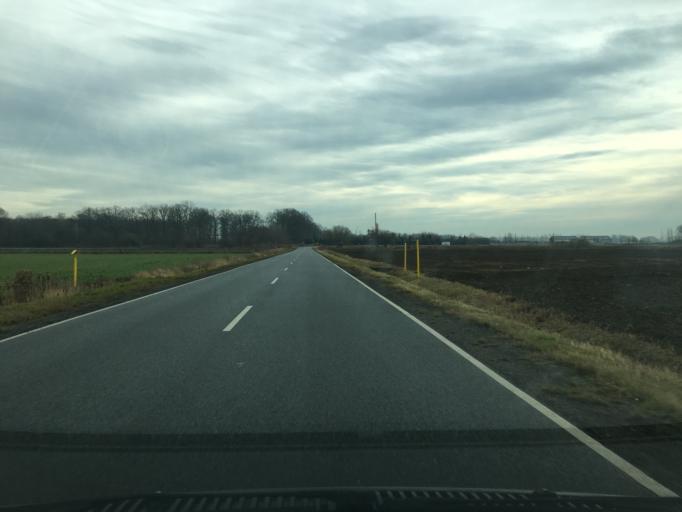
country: PL
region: Lower Silesian Voivodeship
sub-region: Powiat wroclawski
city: Dlugoleka
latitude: 51.1738
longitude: 17.2236
